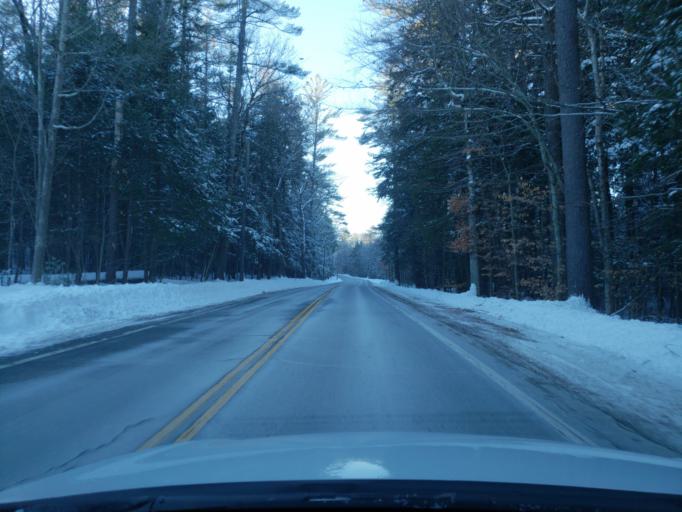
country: US
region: New Hampshire
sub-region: Hillsborough County
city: New Boston
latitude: 42.9875
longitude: -71.6745
